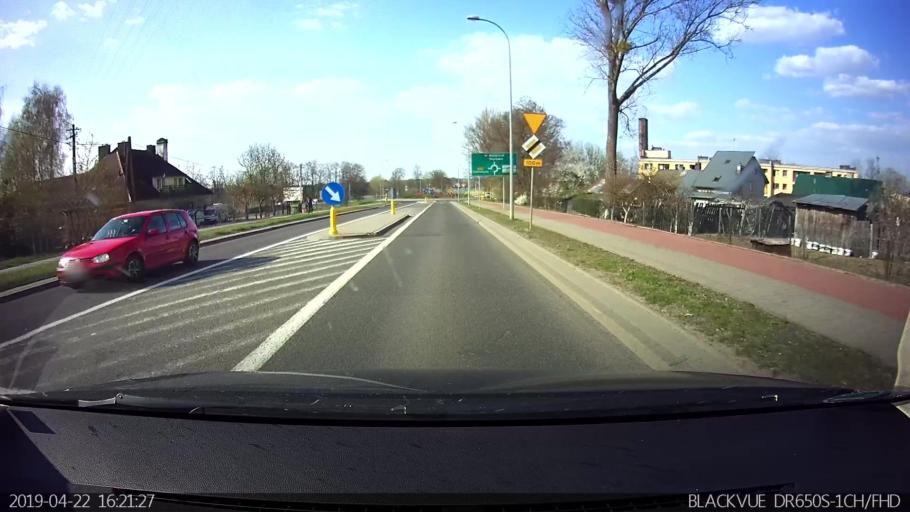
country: PL
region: Podlasie
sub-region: Powiat hajnowski
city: Kleszczele
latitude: 52.5625
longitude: 23.3179
